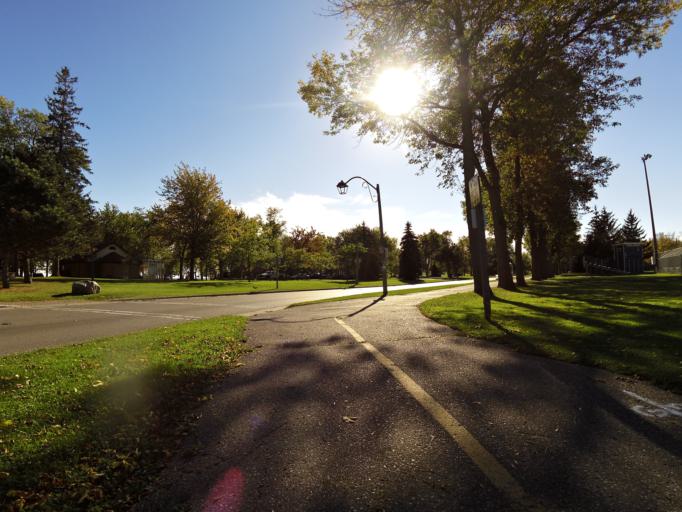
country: CA
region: Ontario
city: Oshawa
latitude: 43.8635
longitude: -78.8290
